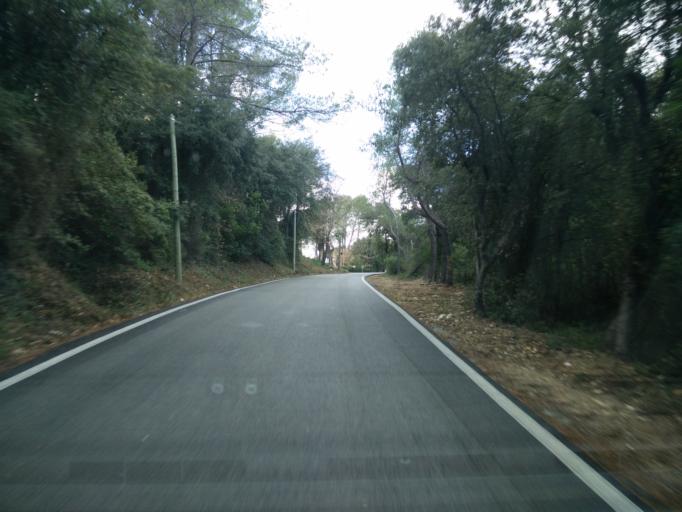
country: FR
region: Provence-Alpes-Cote d'Azur
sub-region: Departement du Var
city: Bagnols-en-Foret
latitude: 43.5495
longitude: 6.6958
